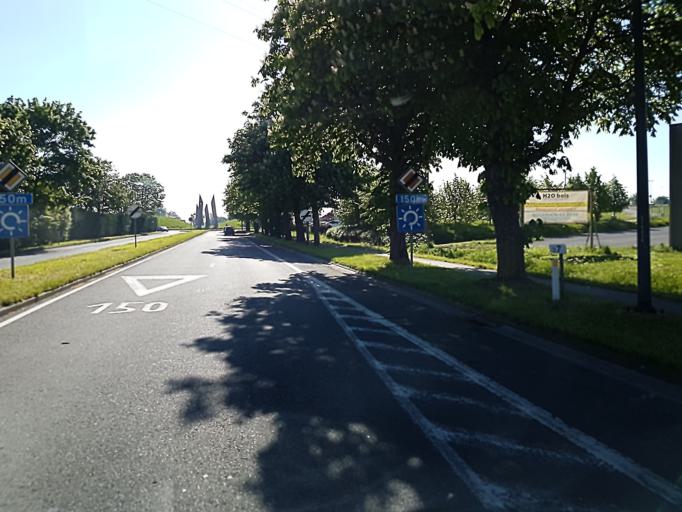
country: BE
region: Wallonia
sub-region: Province du Hainaut
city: Estaimpuis
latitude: 50.7412
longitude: 3.2535
